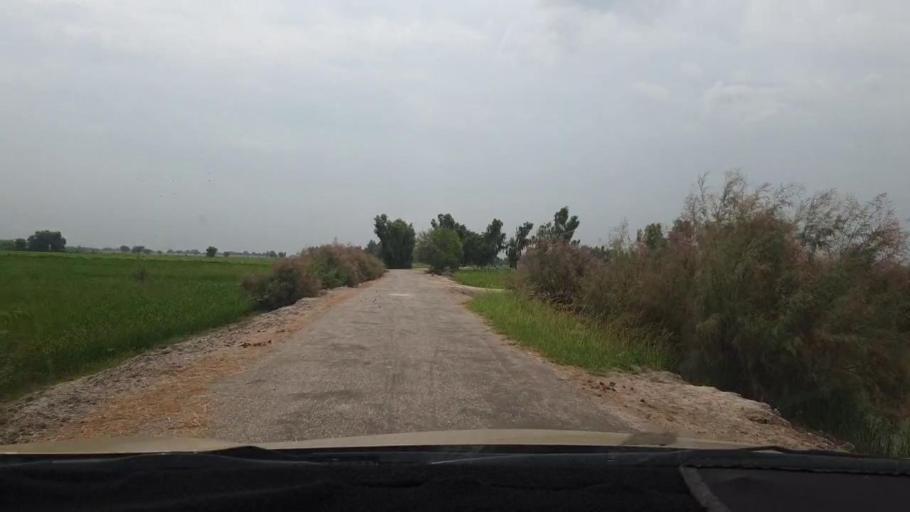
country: PK
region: Sindh
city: Naudero
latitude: 27.6253
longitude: 68.3229
